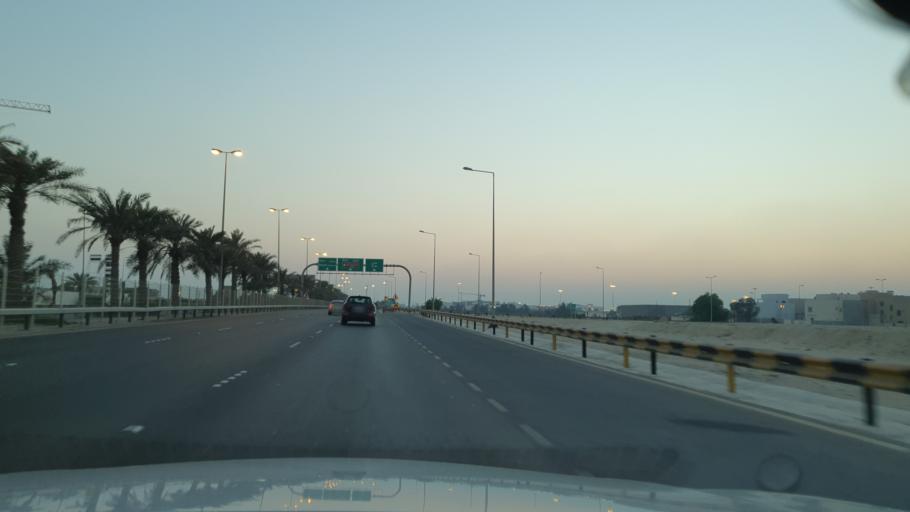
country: BH
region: Northern
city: Madinat `Isa
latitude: 26.1621
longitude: 50.5405
